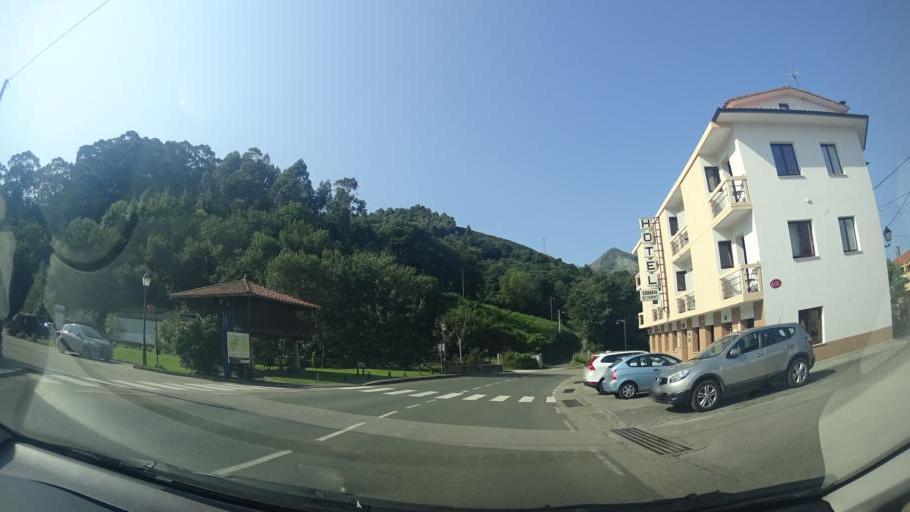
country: ES
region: Asturias
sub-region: Province of Asturias
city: Colunga
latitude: 43.4619
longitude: -5.1872
